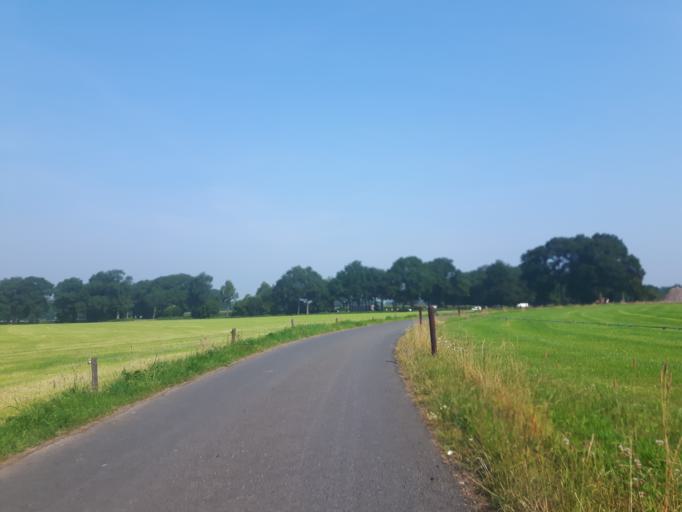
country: NL
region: Overijssel
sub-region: Gemeente Haaksbergen
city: Haaksbergen
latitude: 52.2054
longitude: 6.7383
